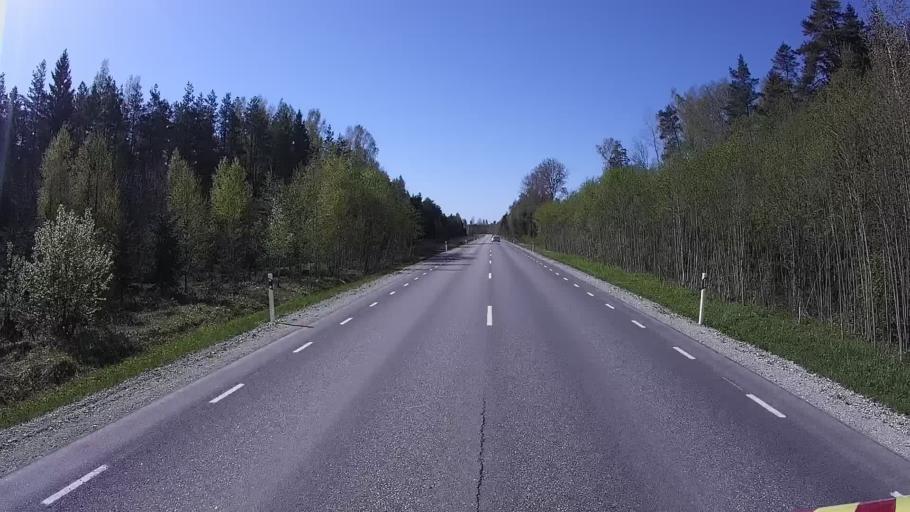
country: EE
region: Raplamaa
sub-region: Jaervakandi vald
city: Jarvakandi
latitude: 58.7638
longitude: 24.8145
